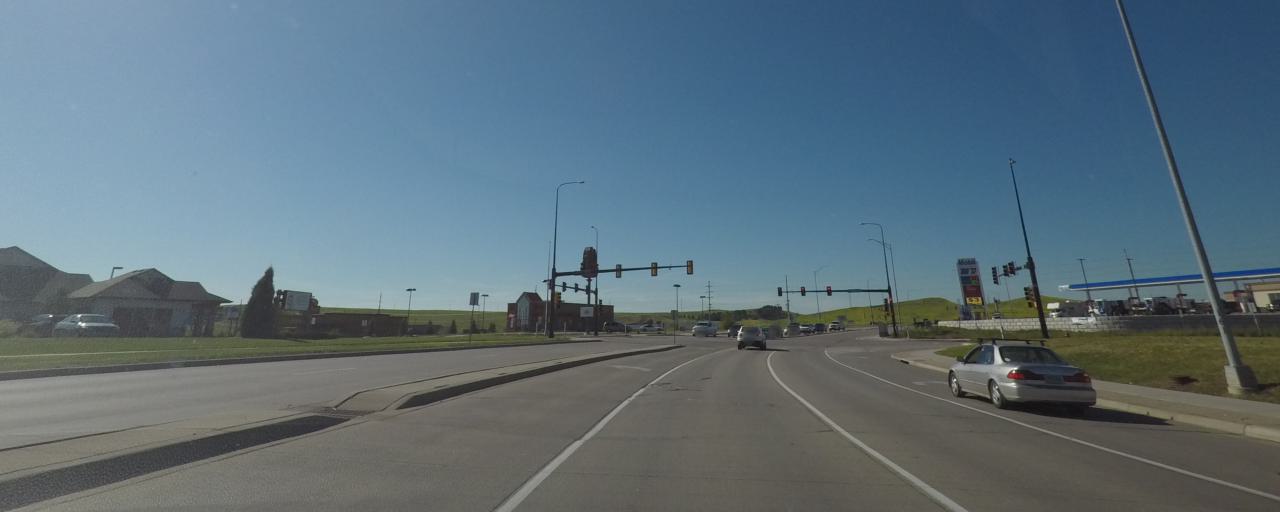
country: US
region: South Dakota
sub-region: Pennington County
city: Rapid City
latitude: 44.0336
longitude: -103.2123
